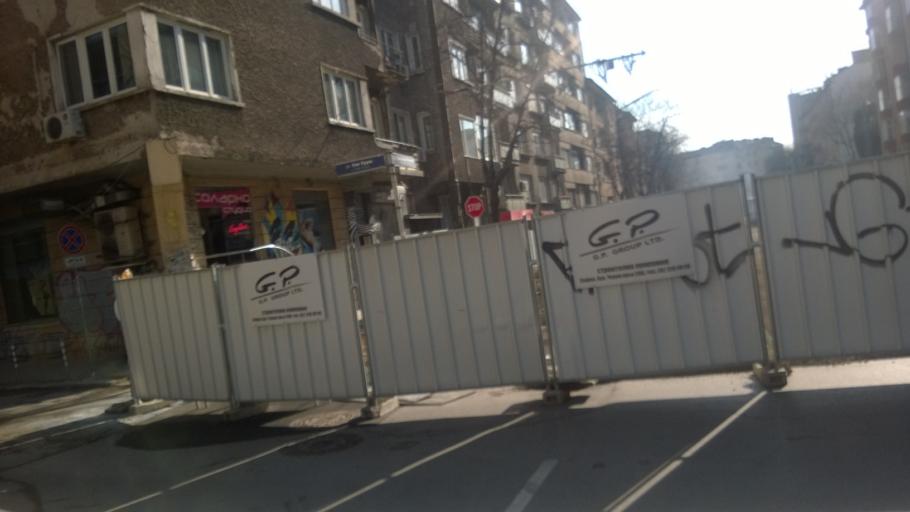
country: BG
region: Sofia-Capital
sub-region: Stolichna Obshtina
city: Sofia
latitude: 42.6886
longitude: 23.3261
